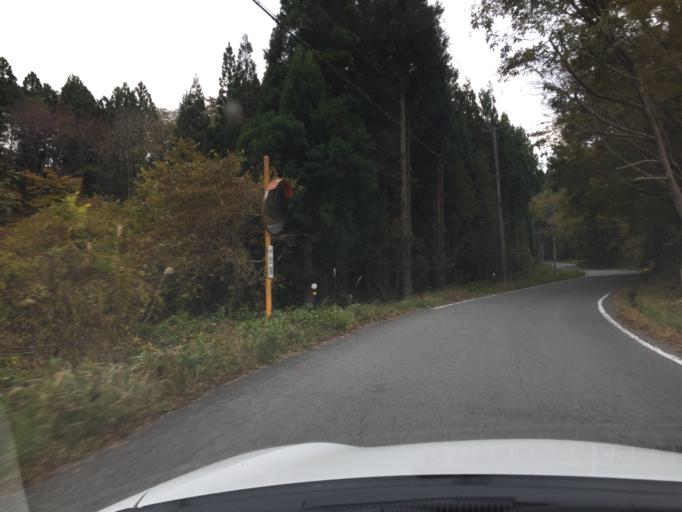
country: JP
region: Fukushima
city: Iwaki
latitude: 37.1169
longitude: 140.7793
